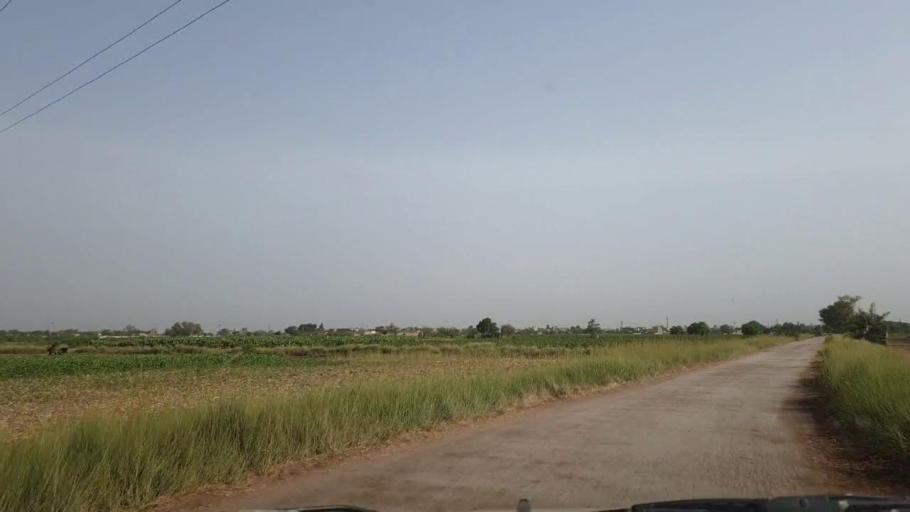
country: PK
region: Sindh
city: Nawabshah
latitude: 26.2253
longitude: 68.4053
